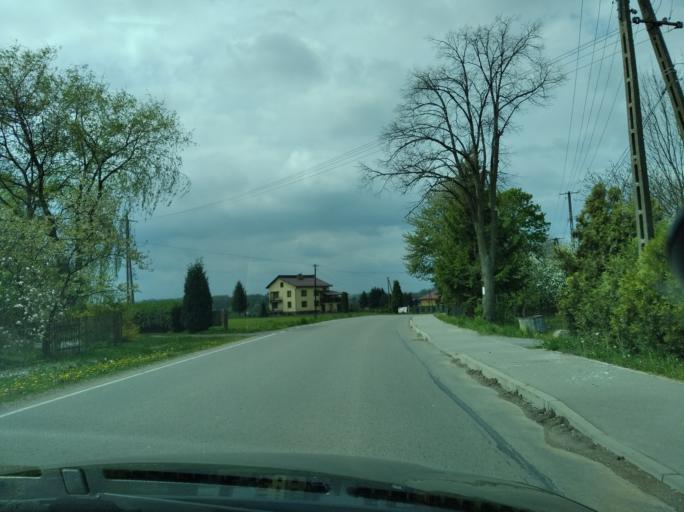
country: PL
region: Subcarpathian Voivodeship
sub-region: Powiat brzozowski
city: Haczow
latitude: 49.6449
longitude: 21.9232
